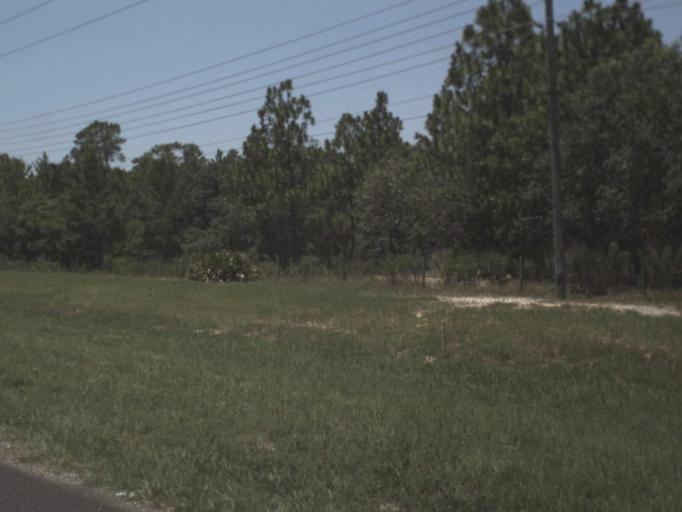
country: US
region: Florida
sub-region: Hernando County
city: Timber Pines
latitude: 28.4898
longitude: -82.6008
